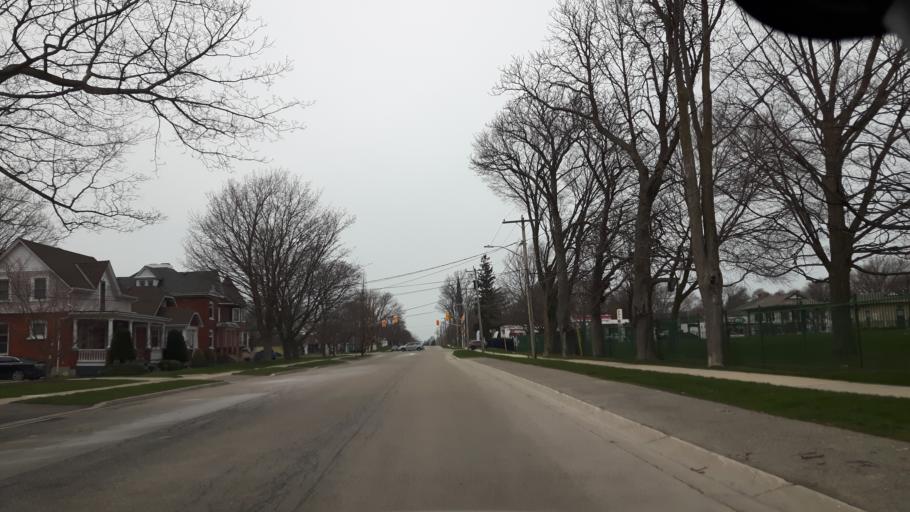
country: CA
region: Ontario
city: Goderich
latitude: 43.7456
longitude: -81.7061
